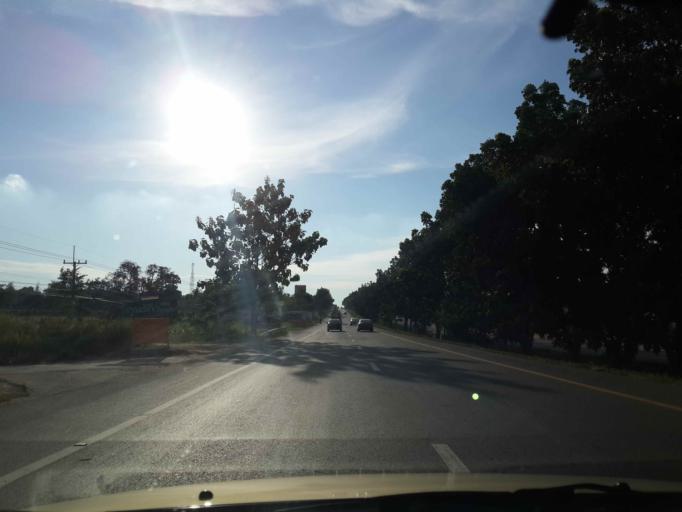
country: TH
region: Chon Buri
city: Bang Lamung
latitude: 12.9800
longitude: 100.9577
